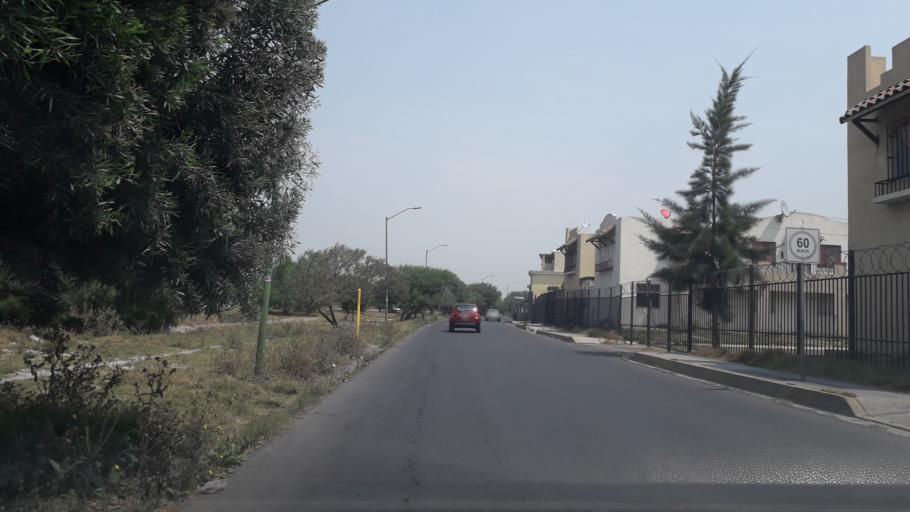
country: MX
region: Mexico
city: Santo Tomas Chiconautla
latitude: 19.6435
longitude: -99.0240
